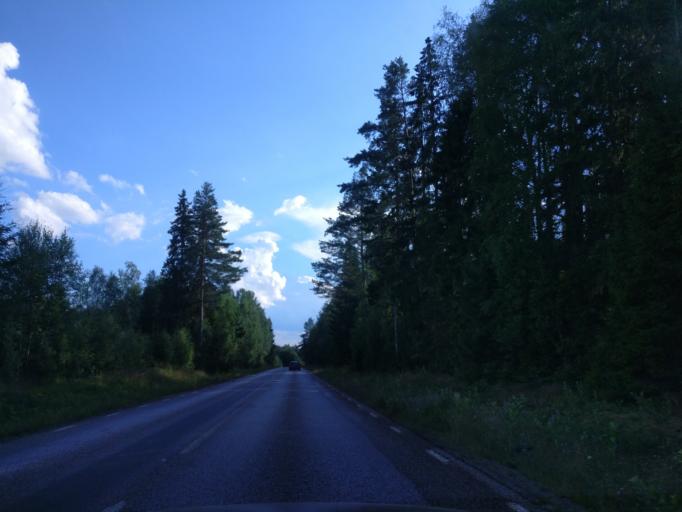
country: SE
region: Dalarna
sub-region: Ludvika Kommun
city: Ludvika
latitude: 60.2682
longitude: 15.0617
